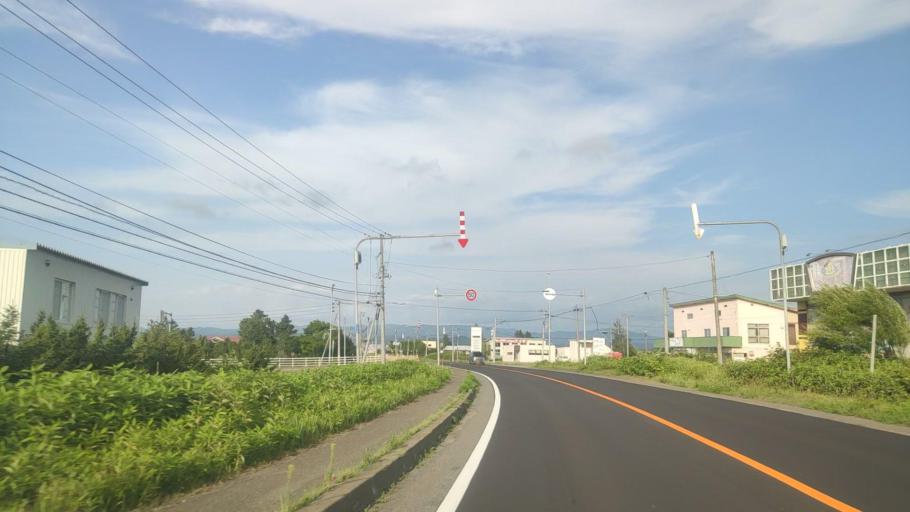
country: JP
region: Hokkaido
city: Iwamizawa
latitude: 43.0161
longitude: 141.7924
